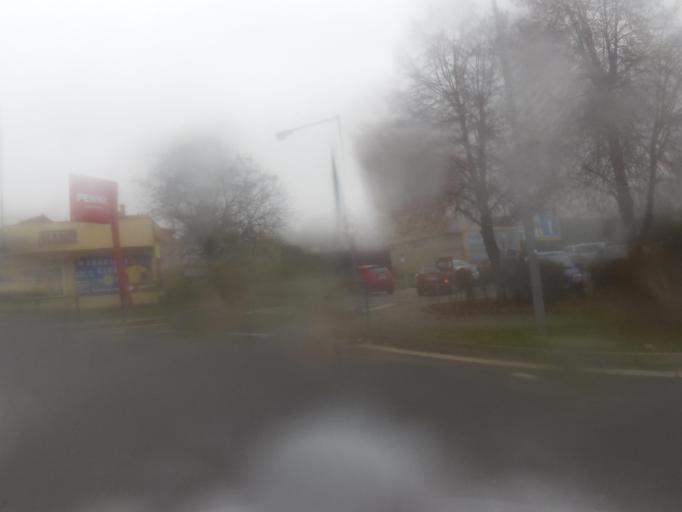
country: CZ
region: Ustecky
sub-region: Okres Louny
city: Louny
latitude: 50.3549
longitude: 13.8071
